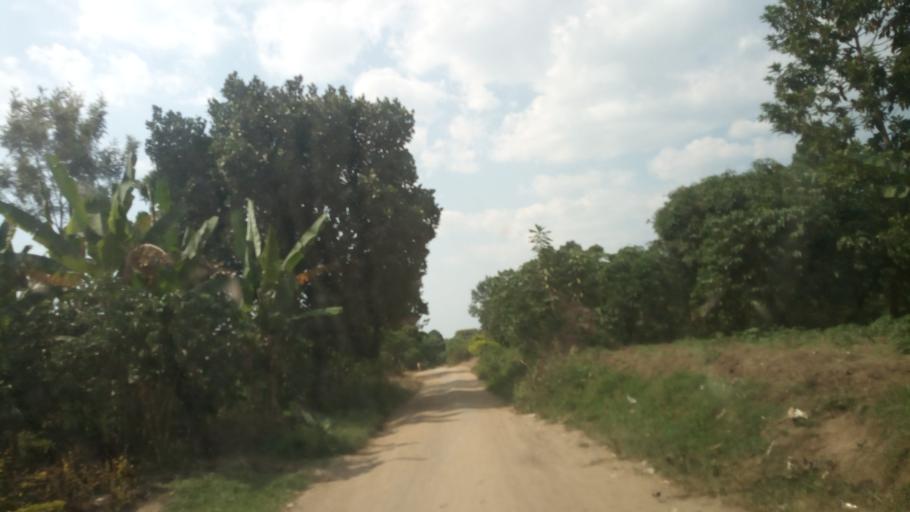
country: UG
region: Western Region
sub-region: Kanungu District
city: Ntungamo
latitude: -0.7869
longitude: 29.6887
